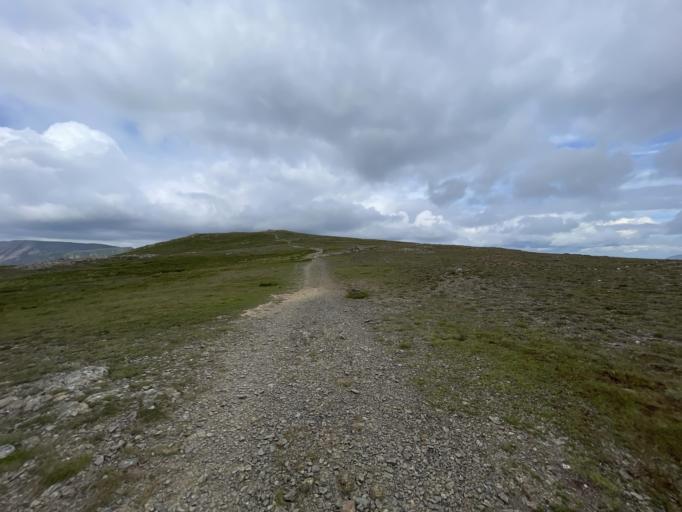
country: GB
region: England
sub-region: Cumbria
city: Keswick
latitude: 54.5382
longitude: -3.2352
